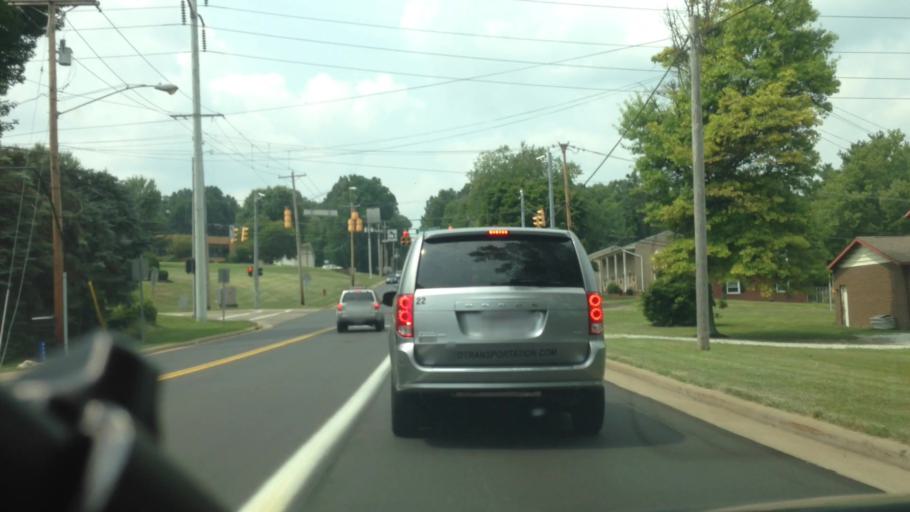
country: US
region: Ohio
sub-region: Stark County
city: Perry Heights
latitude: 40.8112
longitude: -81.4344
